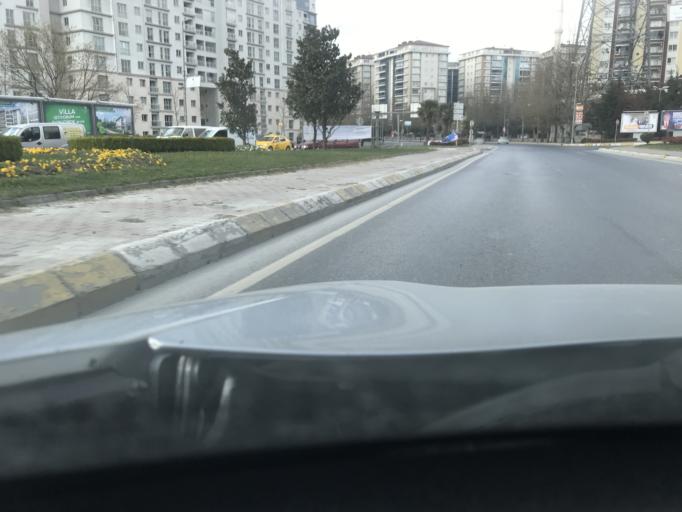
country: TR
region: Istanbul
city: Esenyurt
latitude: 41.0564
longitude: 28.6713
